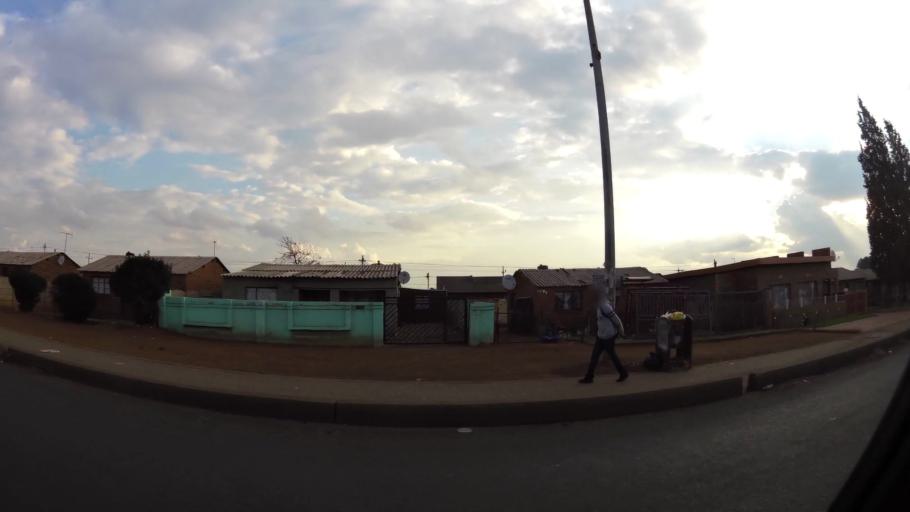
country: ZA
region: Gauteng
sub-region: City of Johannesburg Metropolitan Municipality
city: Orange Farm
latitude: -26.5772
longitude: 27.8409
